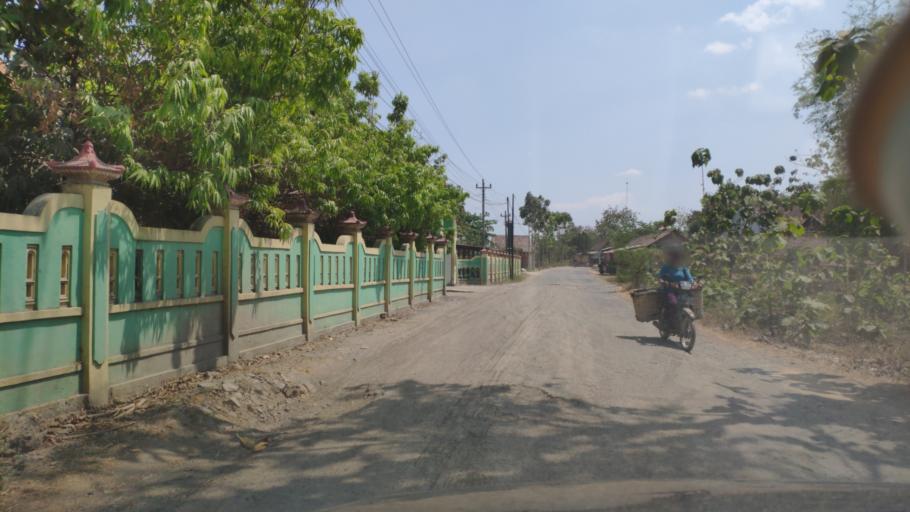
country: ID
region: Central Java
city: Gendangdowo
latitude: -6.9506
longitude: 111.4547
